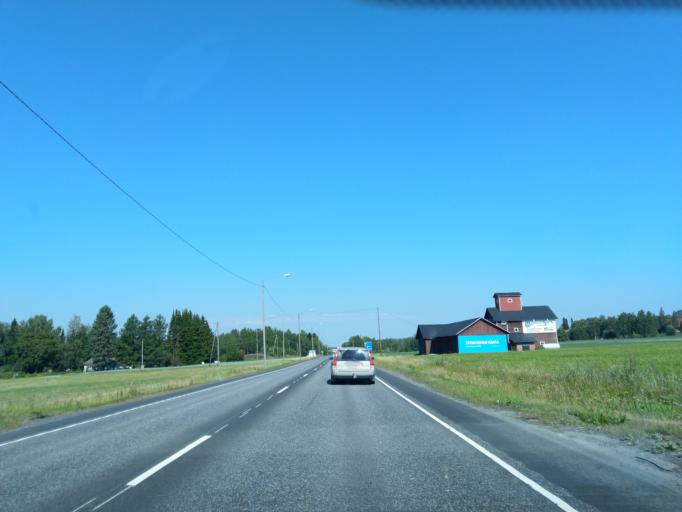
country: FI
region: Satakunta
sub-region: Pori
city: Nakkila
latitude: 61.3563
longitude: 22.0039
